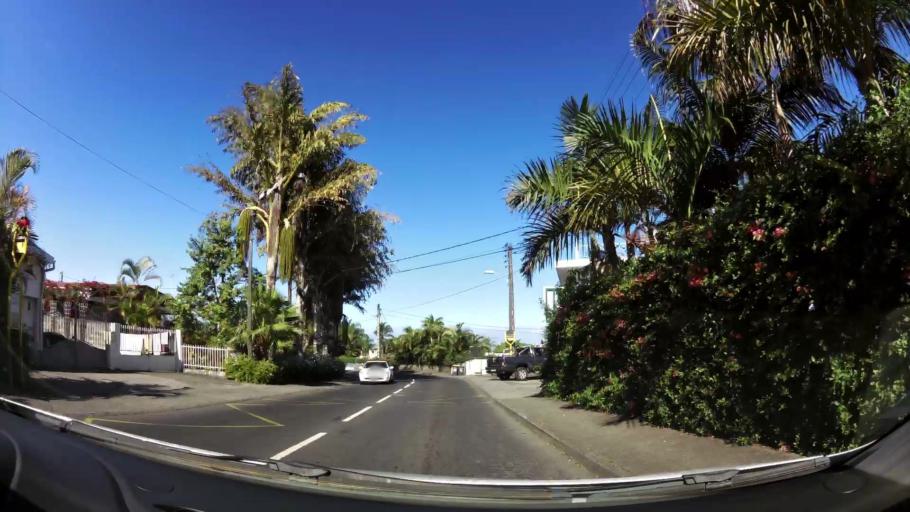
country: RE
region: Reunion
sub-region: Reunion
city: Le Tampon
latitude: -21.2764
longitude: 55.5247
